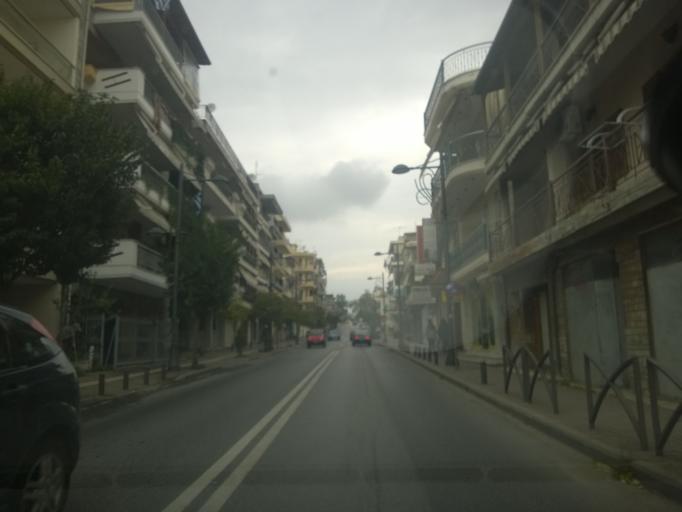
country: GR
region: Central Macedonia
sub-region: Nomos Thessalonikis
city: Stavroupoli
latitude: 40.6672
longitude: 22.9325
